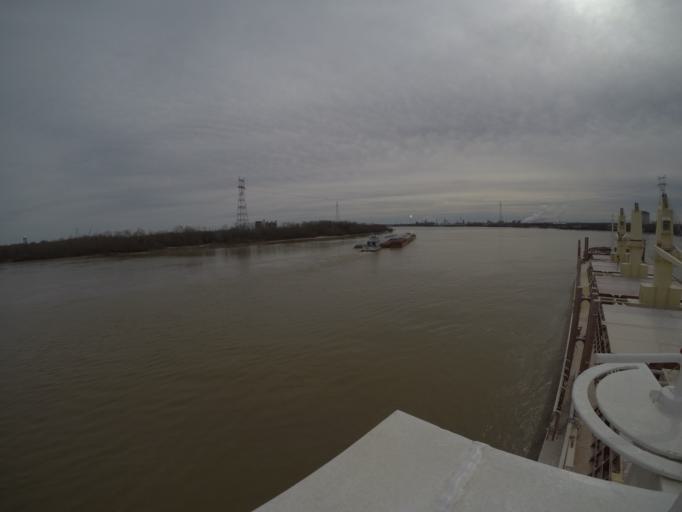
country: US
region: Louisiana
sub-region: Saint Charles Parish
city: Montz
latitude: 30.0061
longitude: -90.4742
